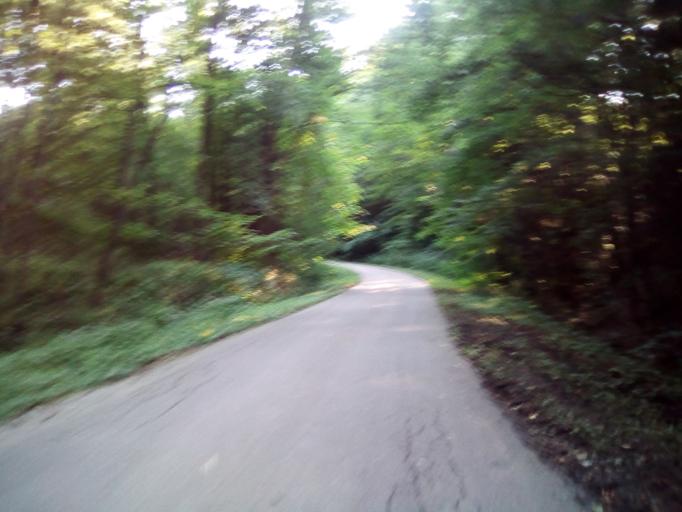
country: PL
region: Subcarpathian Voivodeship
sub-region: Powiat brzozowski
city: Domaradz
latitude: 49.8114
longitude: 21.9651
